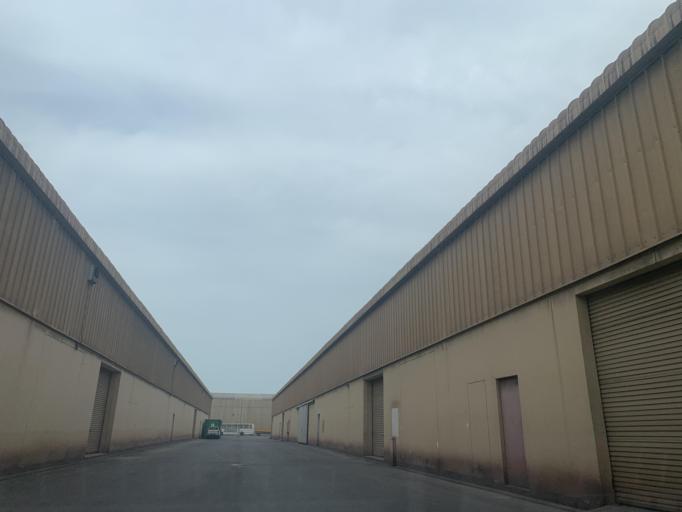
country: BH
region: Muharraq
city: Al Hadd
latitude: 26.2044
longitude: 50.6820
